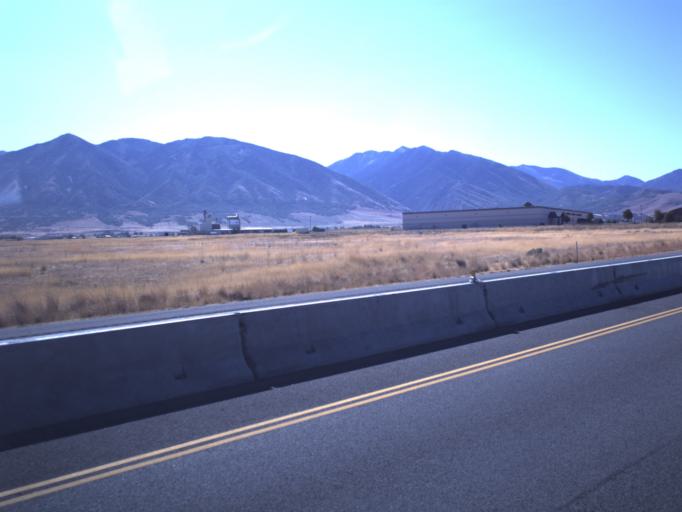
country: US
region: Utah
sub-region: Tooele County
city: Erda
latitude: 40.5791
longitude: -112.2941
